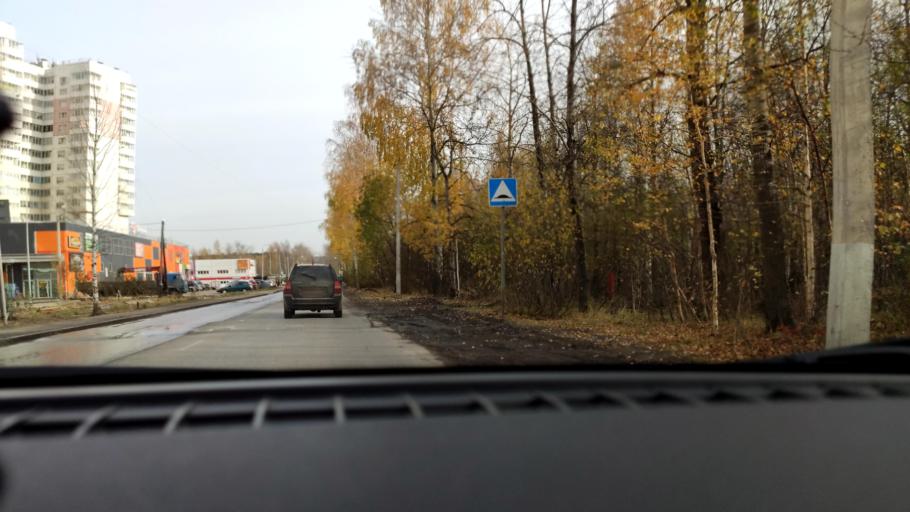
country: RU
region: Perm
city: Polazna
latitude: 58.1324
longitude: 56.3996
